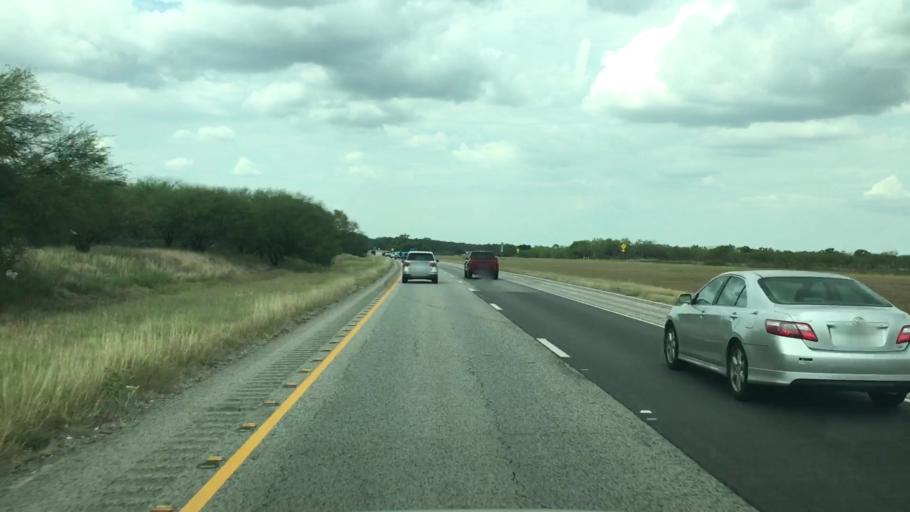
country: US
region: Texas
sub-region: Atascosa County
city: Pleasanton
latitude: 29.0246
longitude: -98.4311
